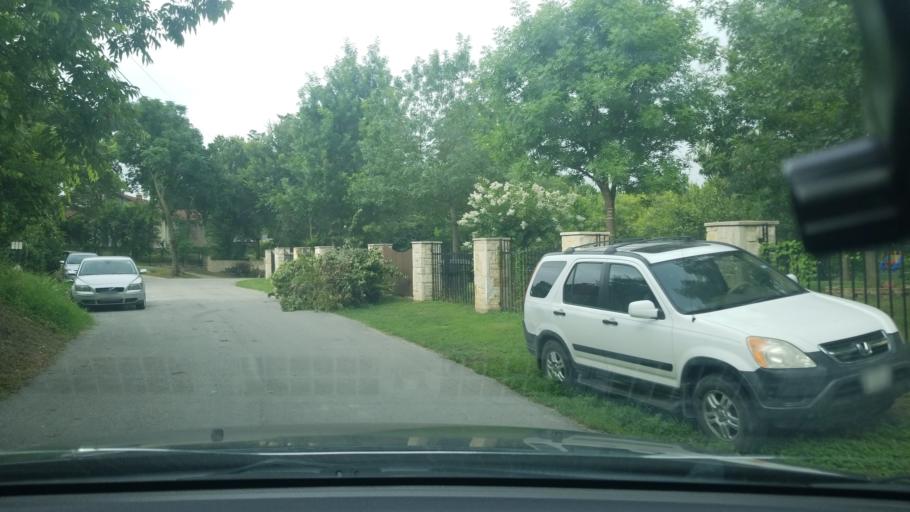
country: US
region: Texas
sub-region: Dallas County
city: Balch Springs
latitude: 32.7730
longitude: -96.6928
